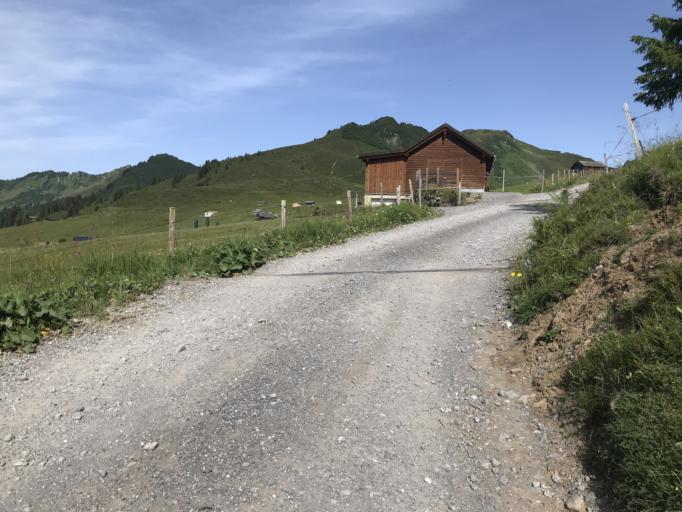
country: AT
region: Vorarlberg
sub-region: Politischer Bezirk Bregenz
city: Damuels
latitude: 47.2819
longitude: 9.8720
